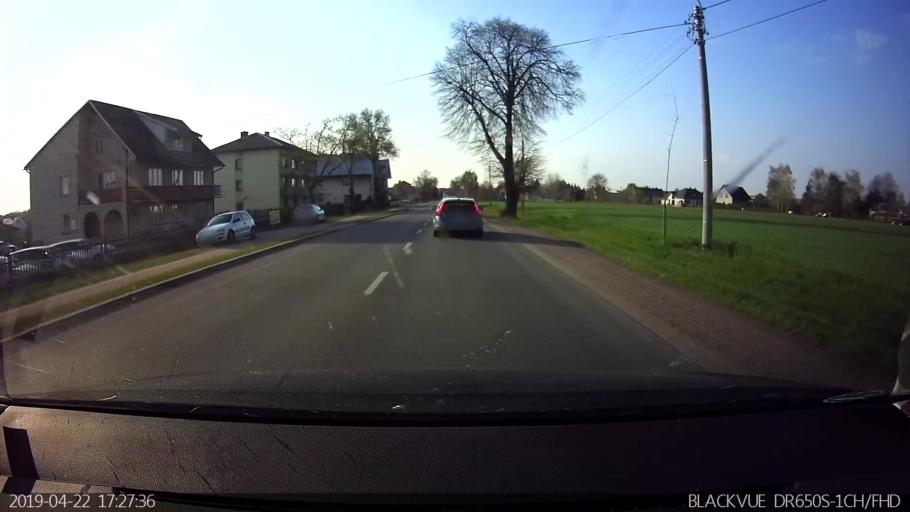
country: PL
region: Masovian Voivodeship
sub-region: Powiat sokolowski
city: Sokolow Podlaski
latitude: 52.3978
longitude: 22.2640
